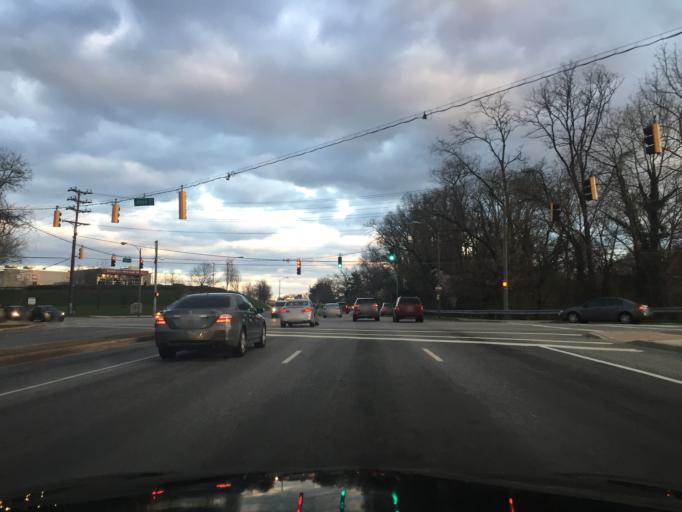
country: US
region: Maryland
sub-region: Baltimore County
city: Towson
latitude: 39.3994
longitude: -76.5872
